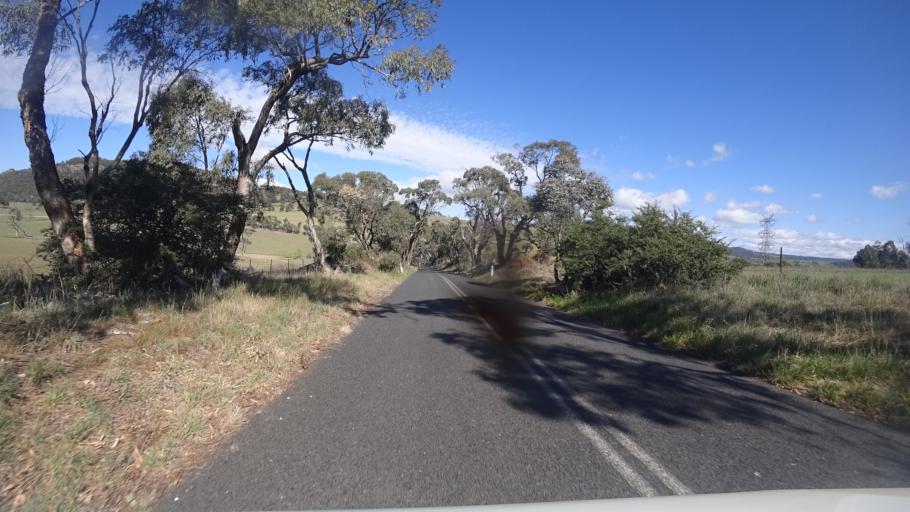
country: AU
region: New South Wales
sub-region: Lithgow
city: Portland
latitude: -33.5232
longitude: 149.9407
